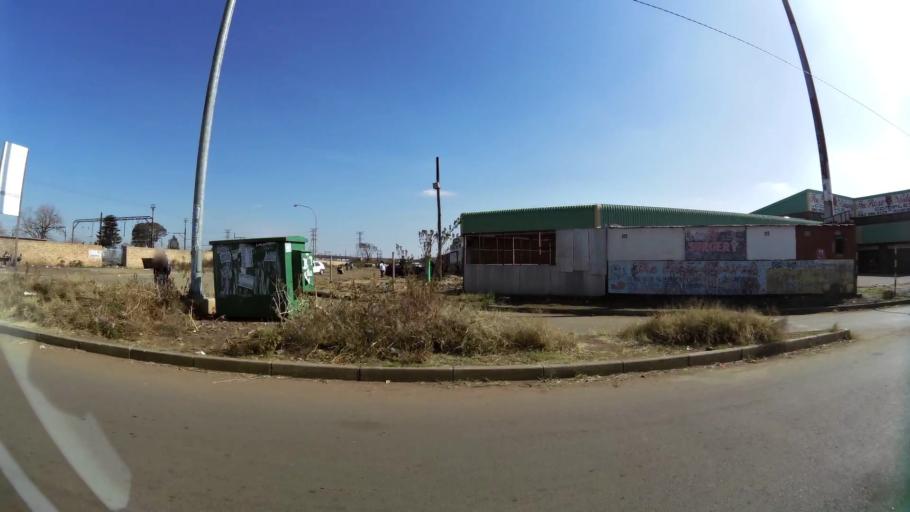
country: ZA
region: Gauteng
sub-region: City of Johannesburg Metropolitan Municipality
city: Soweto
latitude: -26.2925
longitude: 27.8509
